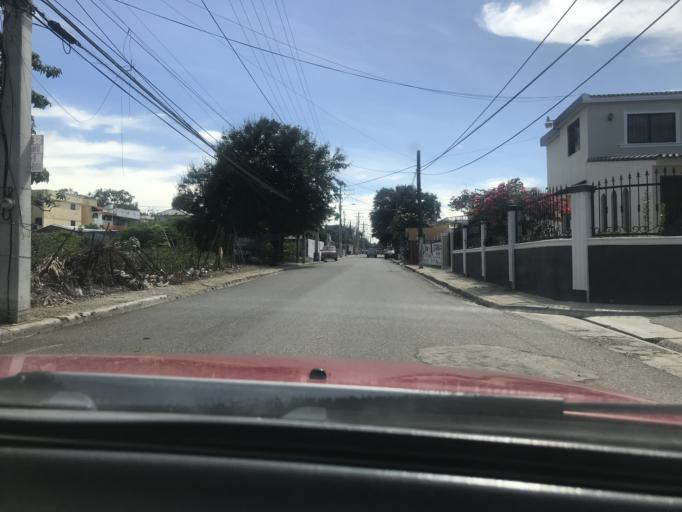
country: DO
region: Santiago
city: Licey al Medio
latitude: 19.4059
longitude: -70.6342
